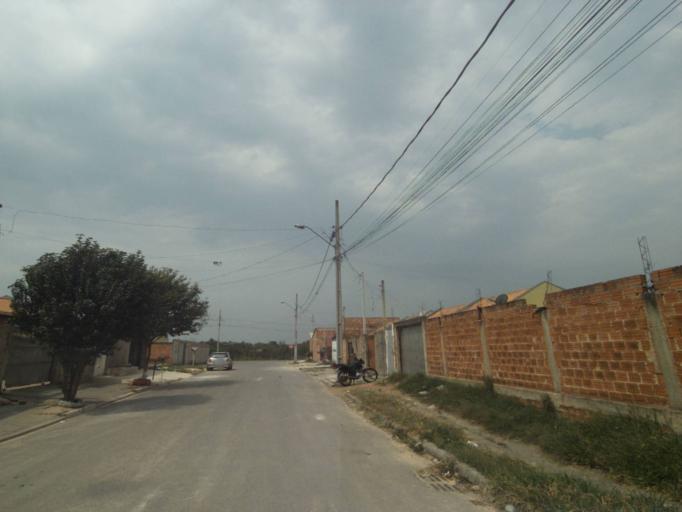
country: BR
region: Parana
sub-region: Sao Jose Dos Pinhais
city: Sao Jose dos Pinhais
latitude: -25.4948
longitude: -49.2000
